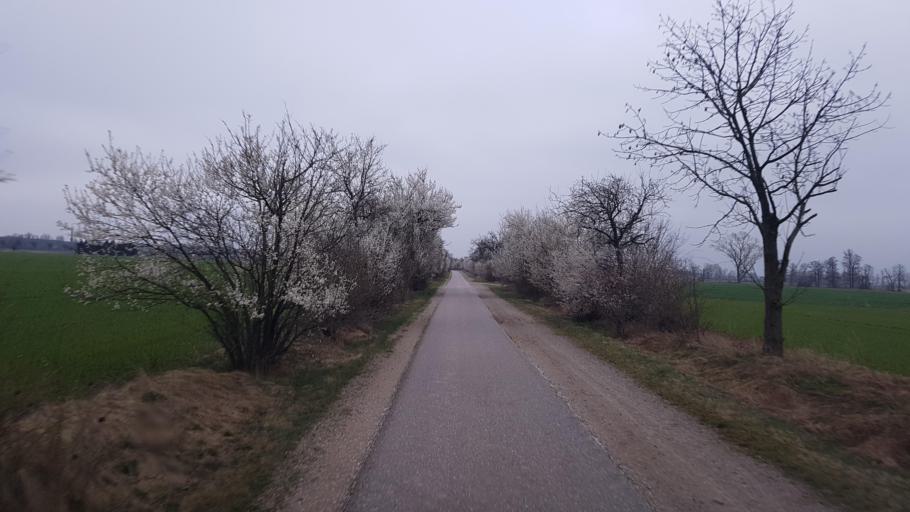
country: DE
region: Brandenburg
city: Bad Liebenwerda
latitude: 51.4750
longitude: 13.3793
